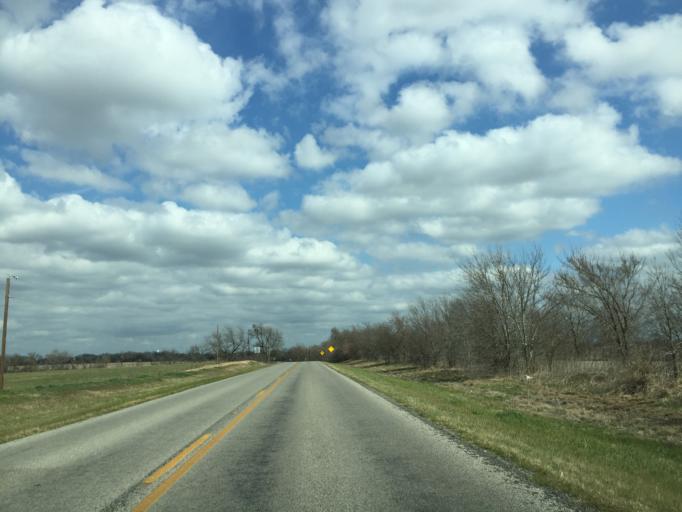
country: US
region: Texas
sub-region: Williamson County
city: Granger
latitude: 30.7054
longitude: -97.4701
